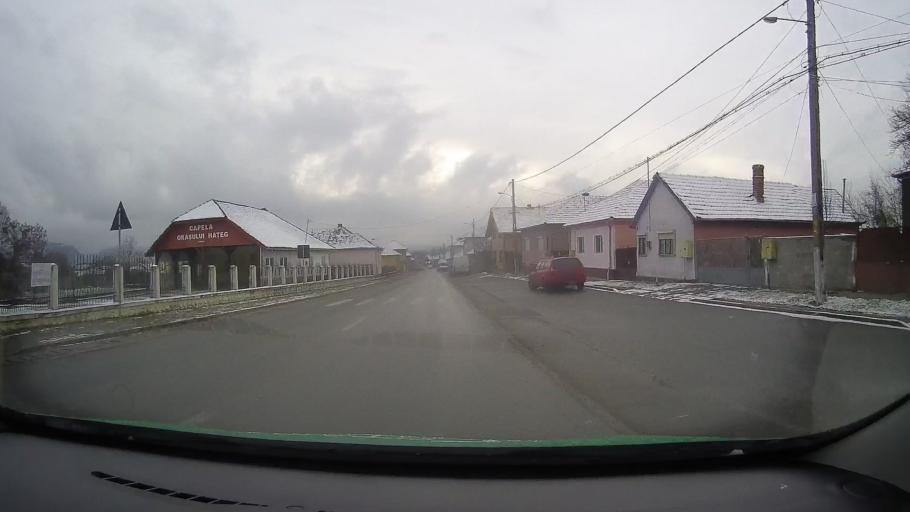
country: RO
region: Hunedoara
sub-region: Oras Hateg
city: Hateg
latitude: 45.6156
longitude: 22.9445
